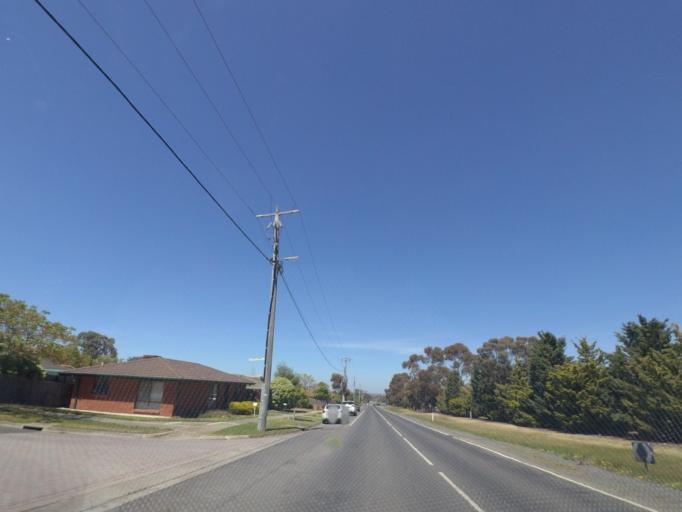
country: AU
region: Victoria
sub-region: Hume
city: Sunbury
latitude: -37.5738
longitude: 144.6943
